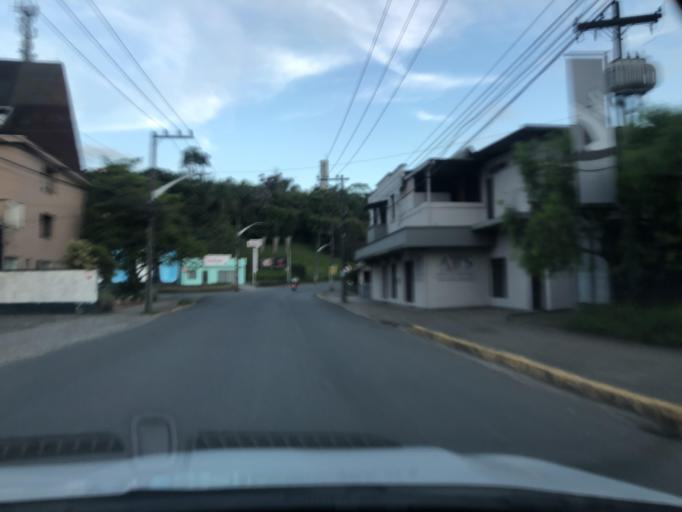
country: BR
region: Santa Catarina
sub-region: Joinville
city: Joinville
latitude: -26.2968
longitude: -48.8629
